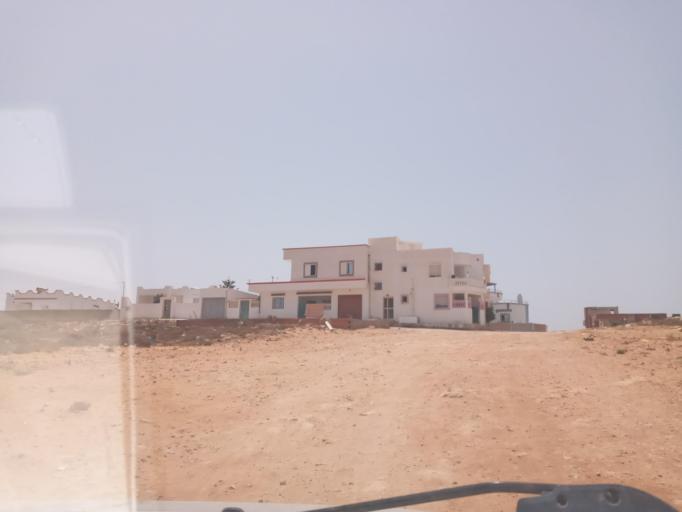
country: TN
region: Nabul
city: El Haouaria
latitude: 37.0549
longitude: 11.0022
